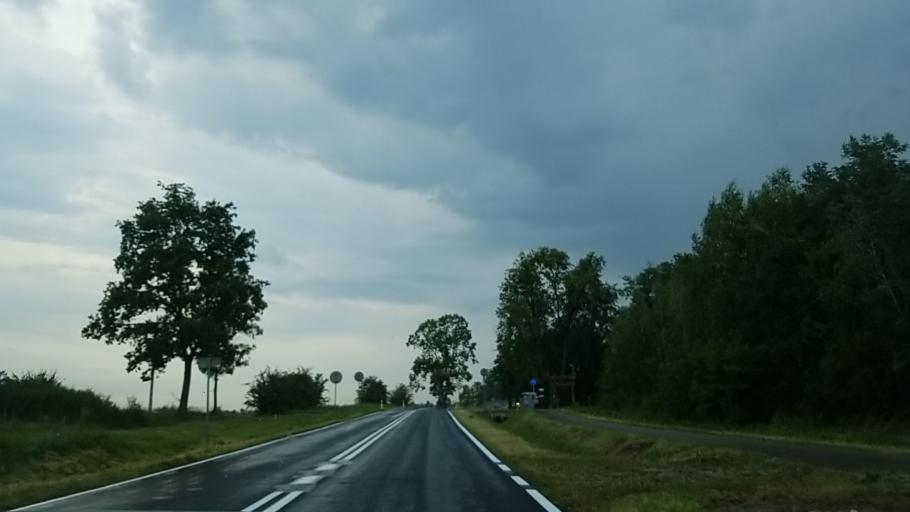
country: PL
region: Lublin Voivodeship
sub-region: Powiat wlodawski
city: Wlodawa
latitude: 51.6065
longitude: 23.5309
